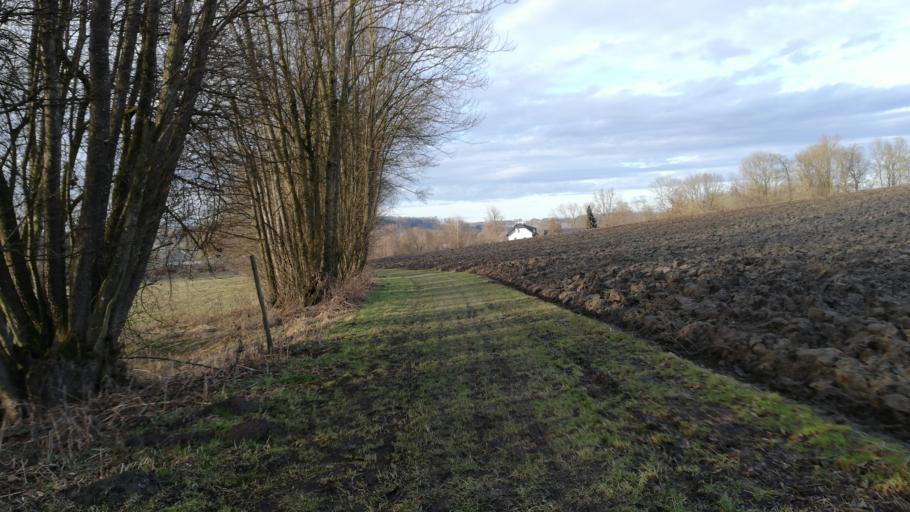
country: AT
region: Upper Austria
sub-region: Politischer Bezirk Grieskirchen
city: Bad Schallerbach
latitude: 48.2007
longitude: 13.9304
